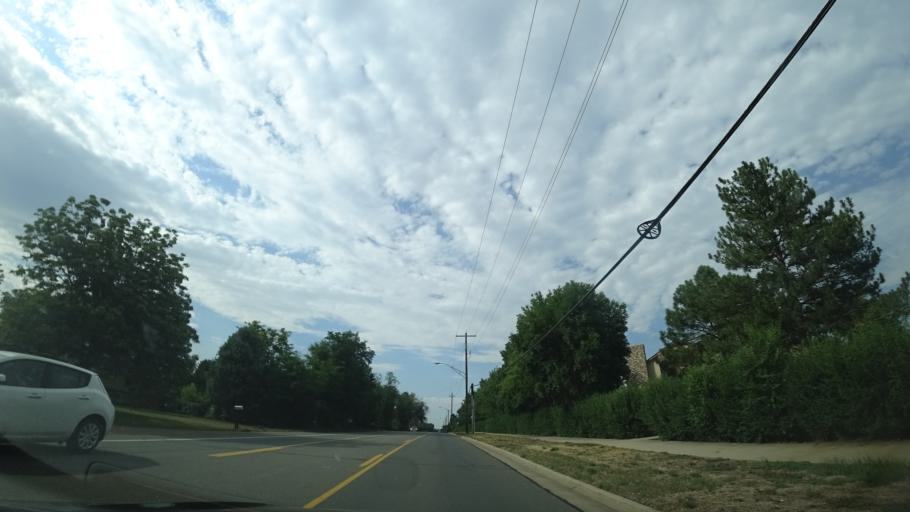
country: US
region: Colorado
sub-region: Jefferson County
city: Lakewood
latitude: 39.7131
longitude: -105.1002
